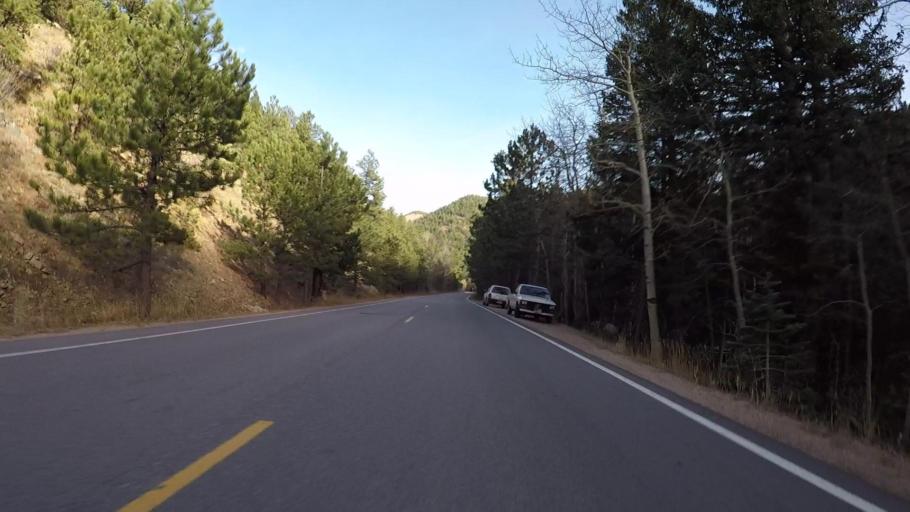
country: US
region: Colorado
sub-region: Boulder County
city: Nederland
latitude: 40.0622
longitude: -105.4698
